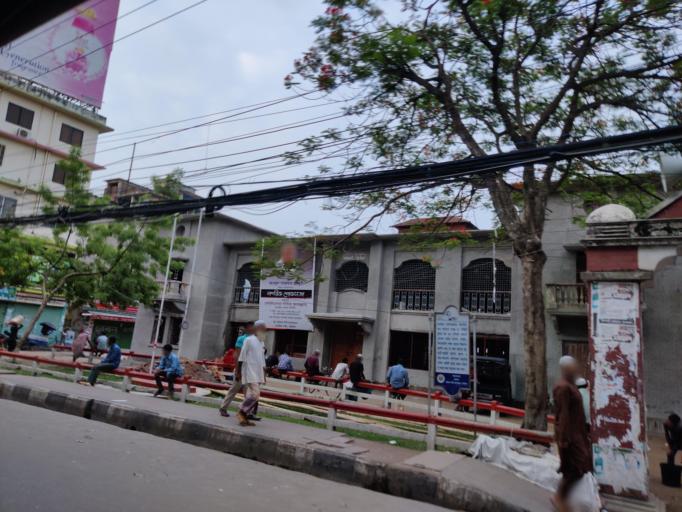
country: BD
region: Barisal
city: Barisal
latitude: 22.7046
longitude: 90.3706
